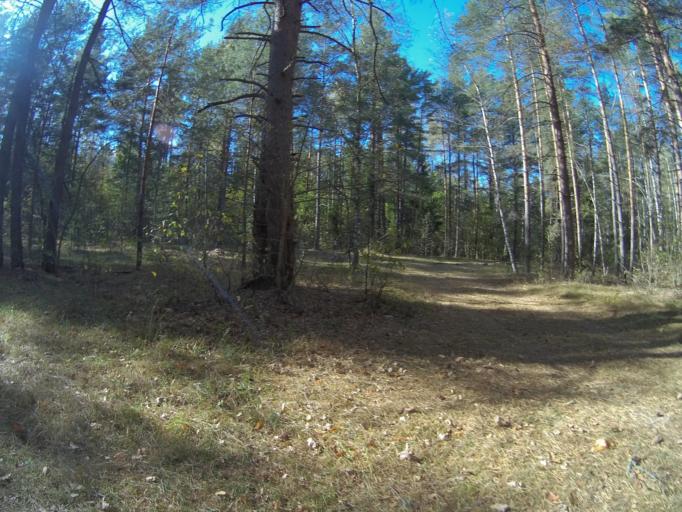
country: RU
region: Vladimir
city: Golovino
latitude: 56.0239
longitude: 40.4790
